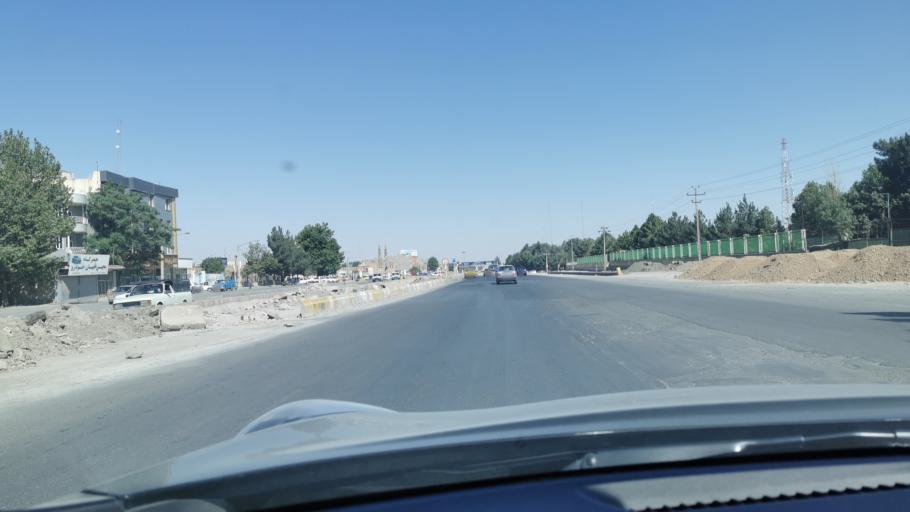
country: IR
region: Razavi Khorasan
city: Chenaran
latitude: 36.6391
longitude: 59.1213
